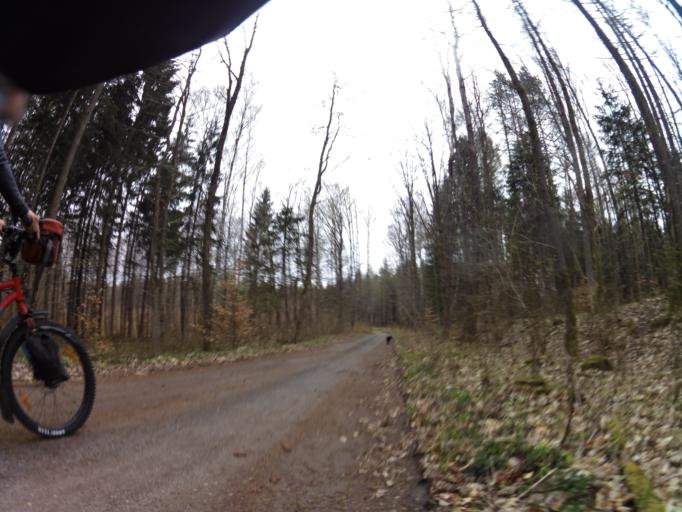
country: PL
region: West Pomeranian Voivodeship
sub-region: Powiat koszalinski
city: Bobolice
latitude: 53.9433
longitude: 16.6856
